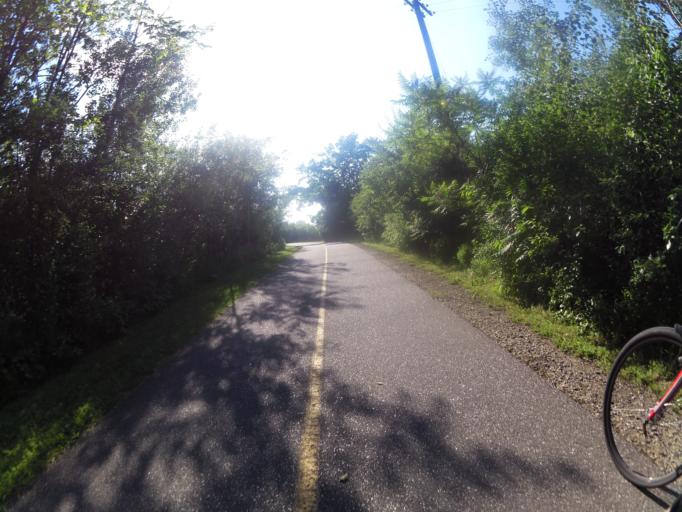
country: CA
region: Ontario
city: Ottawa
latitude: 45.3706
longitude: -75.7447
